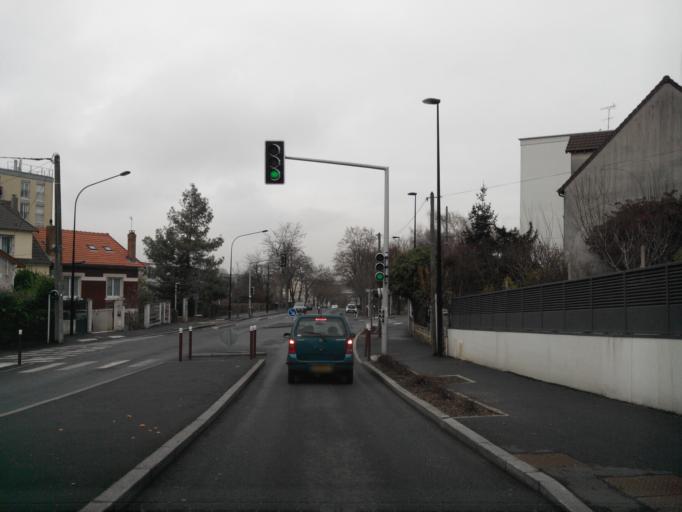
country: FR
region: Ile-de-France
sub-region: Departement du Val-de-Marne
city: L'Hay-les-Roses
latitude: 48.7884
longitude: 2.3370
